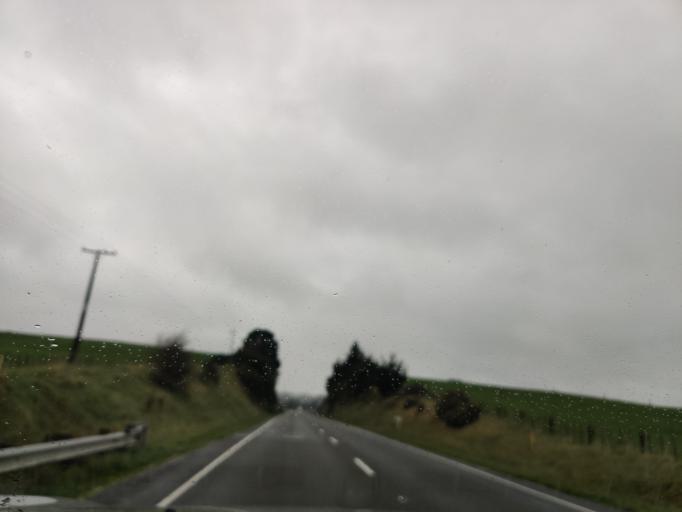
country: NZ
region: Manawatu-Wanganui
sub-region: Palmerston North City
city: Palmerston North
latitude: -40.0603
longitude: 176.2270
